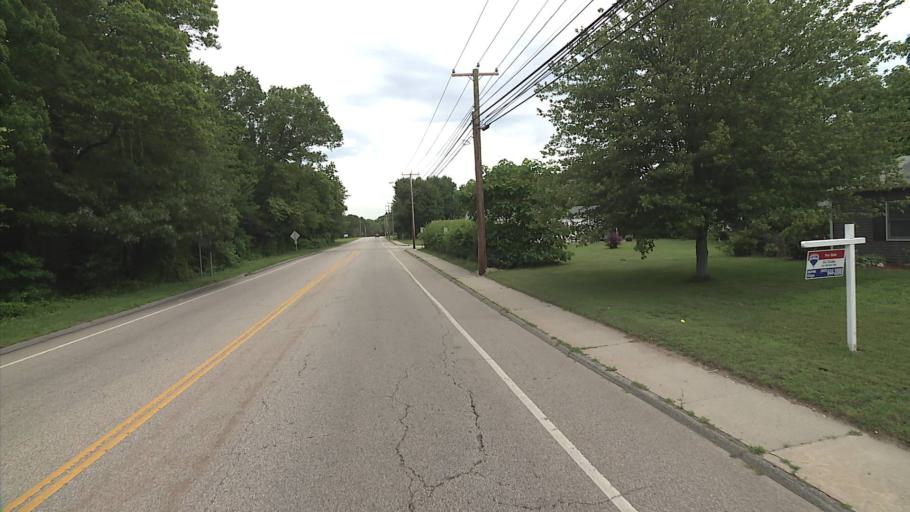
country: US
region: Connecticut
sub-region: New London County
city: Poquonock Bridge
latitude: 41.3499
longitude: -72.0293
